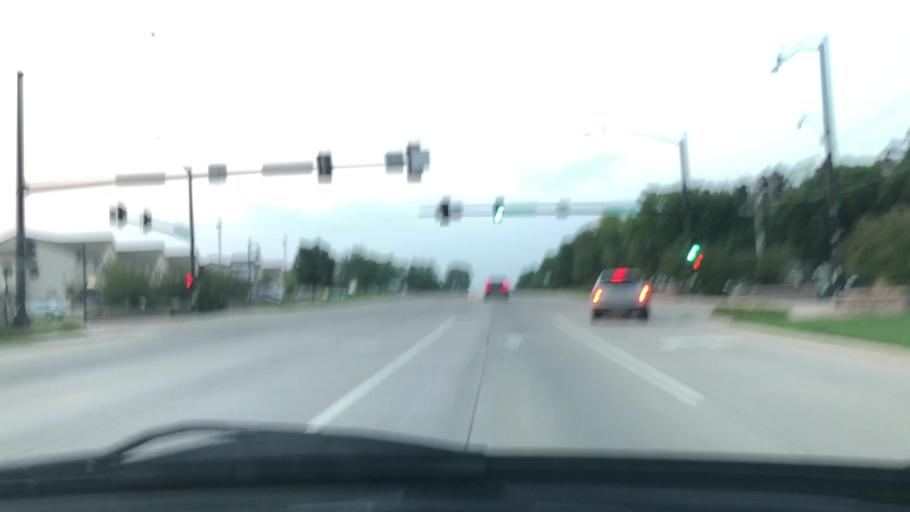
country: US
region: Iowa
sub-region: Johnson County
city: North Liberty
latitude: 41.7374
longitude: -91.6076
